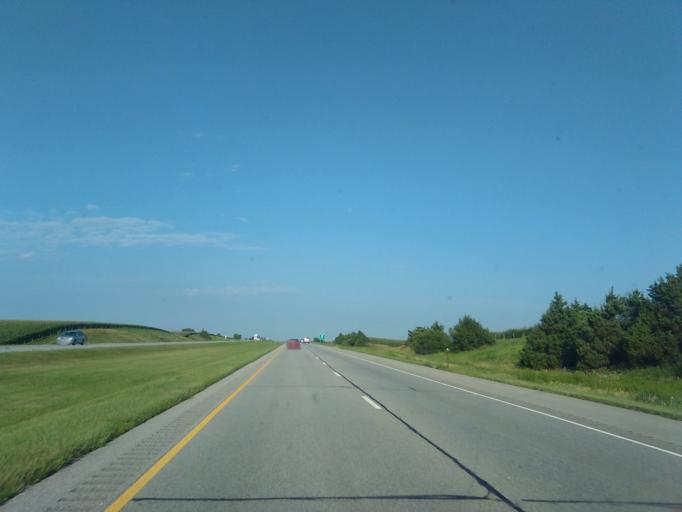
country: US
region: Nebraska
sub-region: Saline County
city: Friend
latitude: 40.8213
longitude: -97.3783
